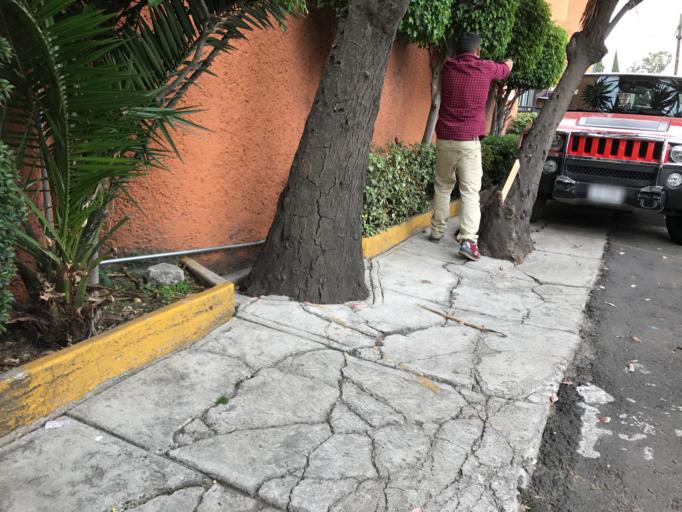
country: MX
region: Mexico City
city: Tlalpan
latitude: 19.2897
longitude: -99.1379
